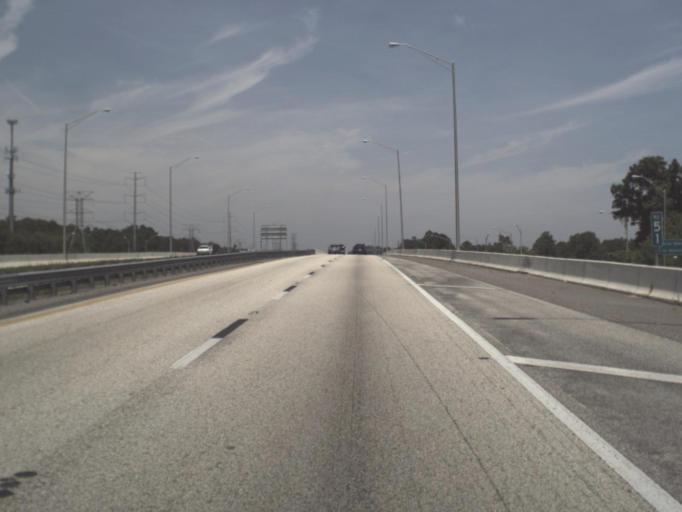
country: US
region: Florida
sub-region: Duval County
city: Neptune Beach
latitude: 30.2852
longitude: -81.5216
